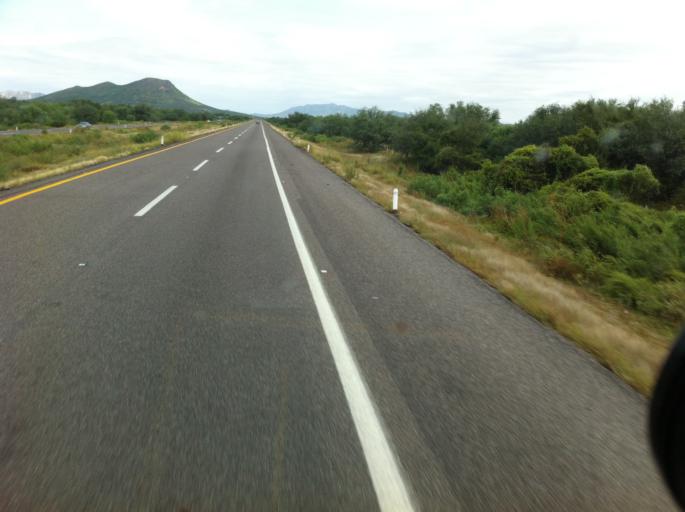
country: MX
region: Sonora
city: Hermosillo
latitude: 28.8512
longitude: -110.9583
